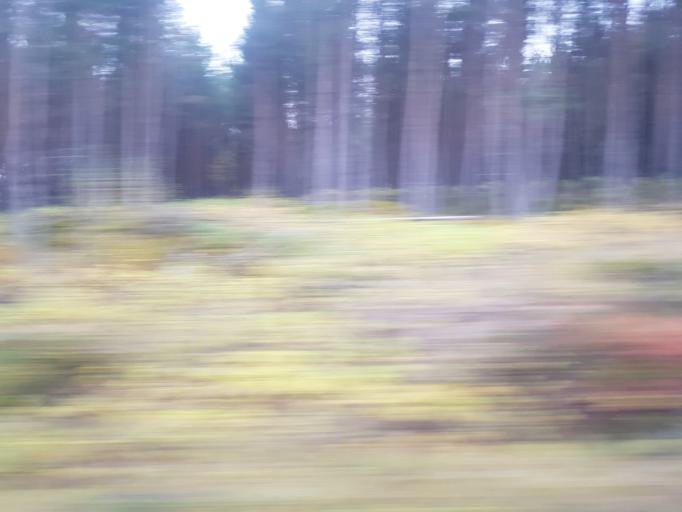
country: NO
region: Oppland
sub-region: Dovre
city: Dovre
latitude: 61.9217
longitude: 9.3457
